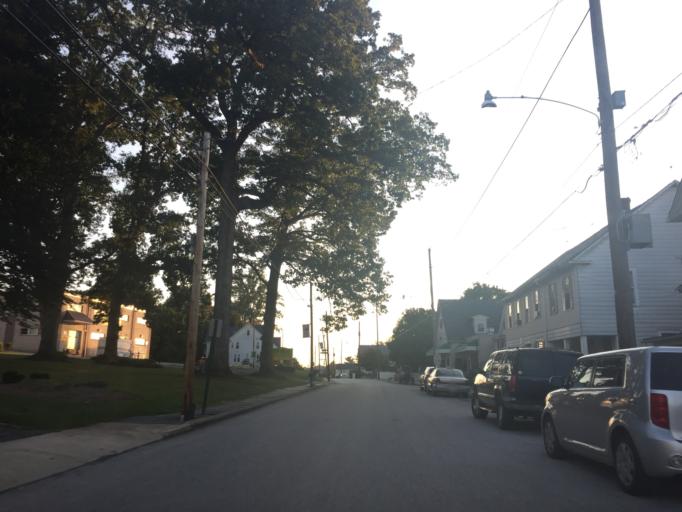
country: US
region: Pennsylvania
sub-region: York County
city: Susquehanna Trails
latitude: 39.7274
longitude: -76.3259
